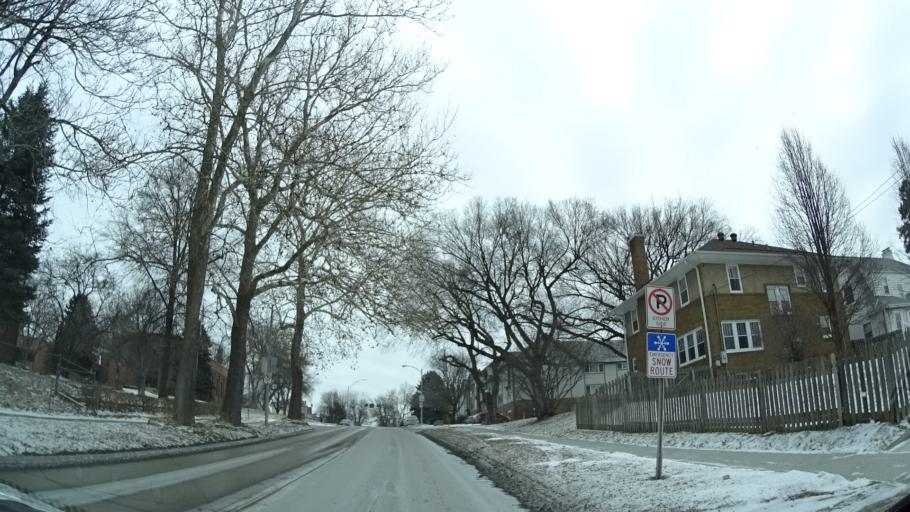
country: US
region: Nebraska
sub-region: Douglas County
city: Omaha
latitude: 41.2578
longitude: -95.9899
